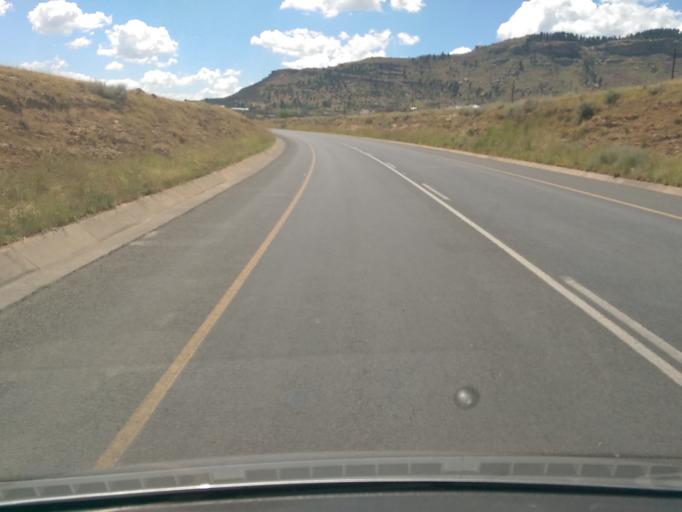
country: LS
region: Maseru
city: Maseru
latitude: -29.3695
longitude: 27.4742
